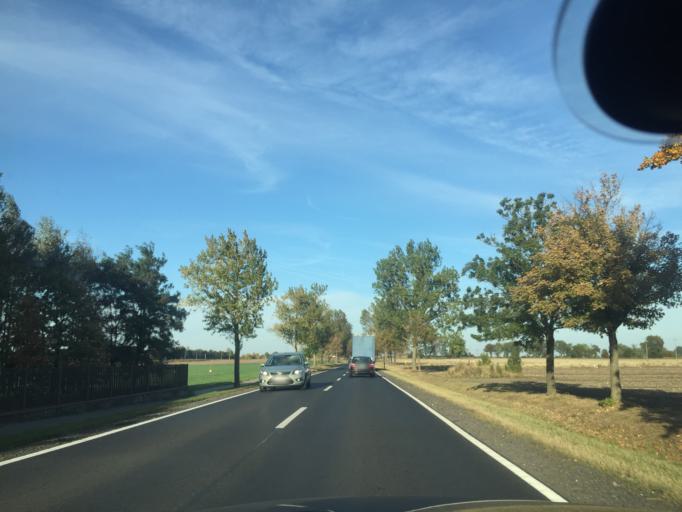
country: PL
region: Kujawsko-Pomorskie
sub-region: Powiat inowroclawski
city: Wierzchoslawice
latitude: 52.8726
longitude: 18.3726
